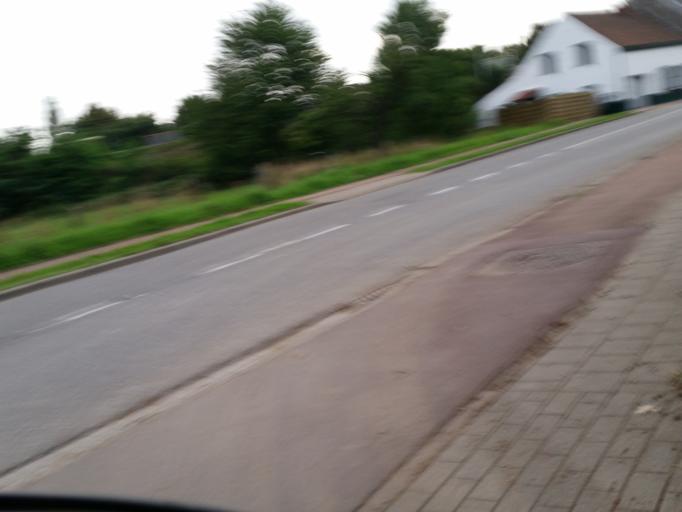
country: BE
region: Flanders
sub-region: Provincie Vlaams-Brabant
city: Zemst
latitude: 50.9580
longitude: 4.4589
